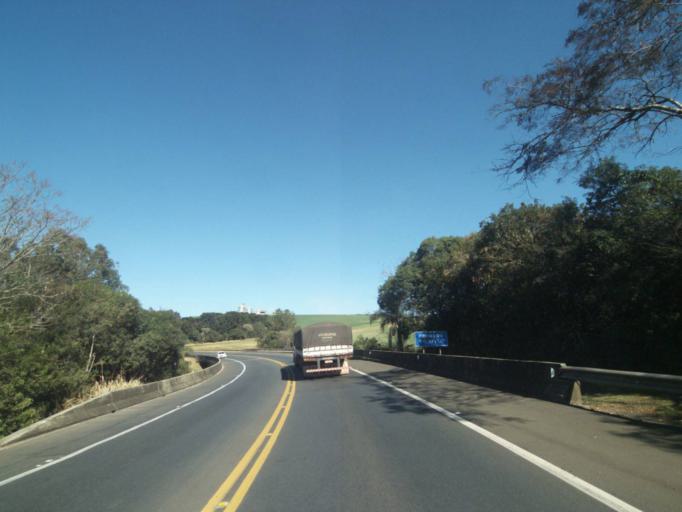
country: BR
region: Parana
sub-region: Tibagi
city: Tibagi
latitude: -24.6960
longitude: -50.5828
